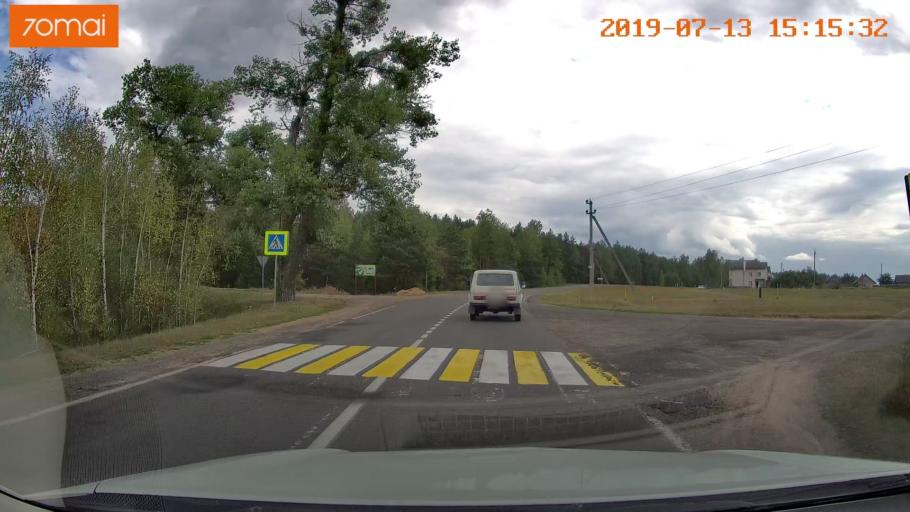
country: BY
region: Mogilev
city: Hlusha
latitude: 53.1161
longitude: 28.8279
